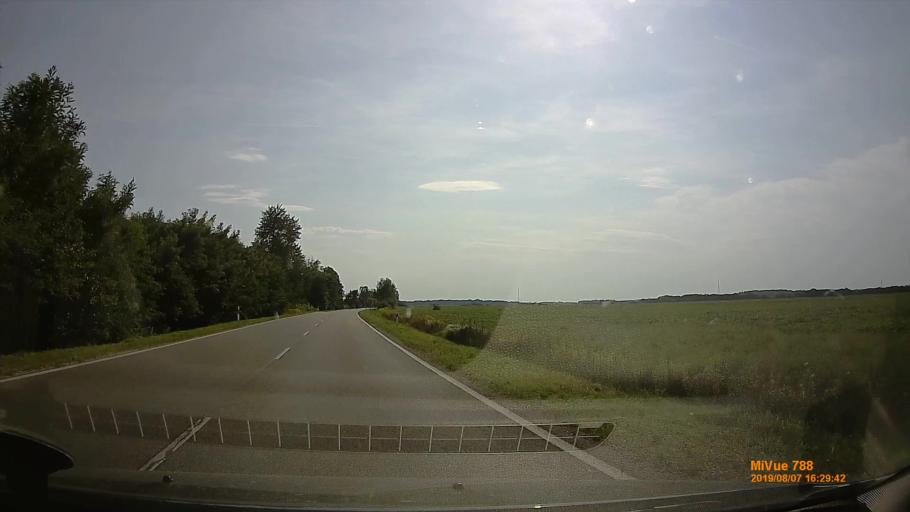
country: HU
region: Zala
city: Lenti
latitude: 46.6775
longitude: 16.5250
